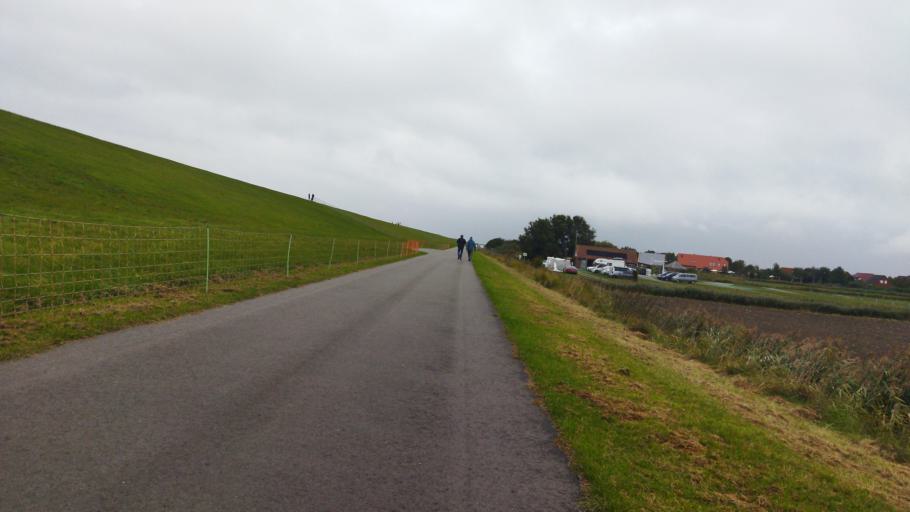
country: NL
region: Groningen
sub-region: Gemeente Delfzijl
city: Delfzijl
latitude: 53.4176
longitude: 7.0135
